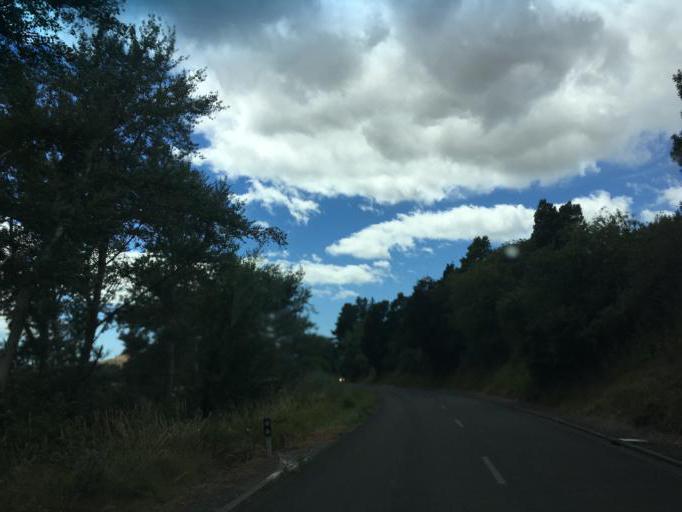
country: NZ
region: Hawke's Bay
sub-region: Hastings District
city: Hastings
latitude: -39.7349
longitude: 176.9014
